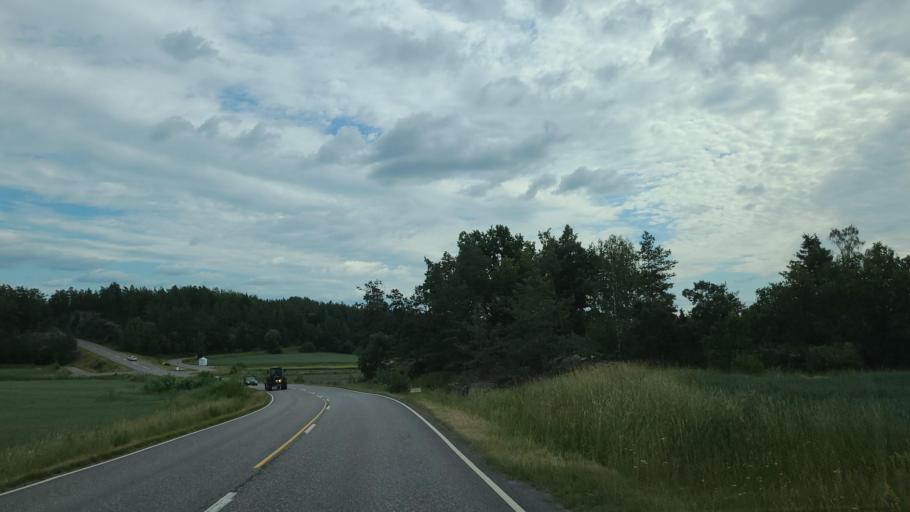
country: FI
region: Varsinais-Suomi
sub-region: Turku
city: Rymaettylae
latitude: 60.3665
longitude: 21.9463
